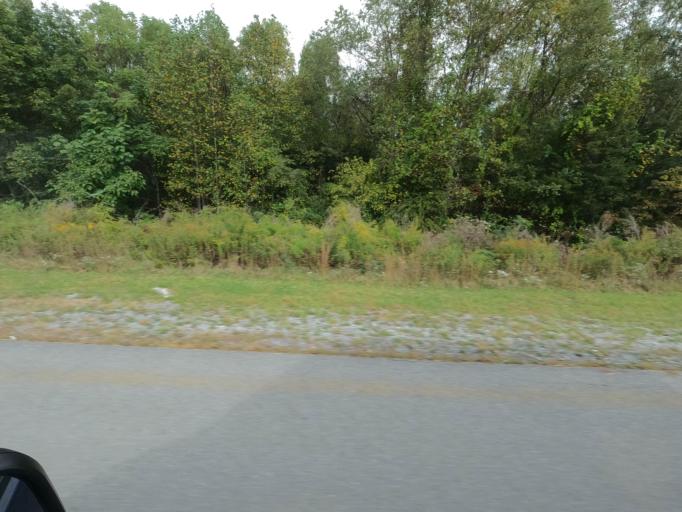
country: US
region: Tennessee
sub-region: Carter County
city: Central
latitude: 36.3247
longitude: -82.2585
